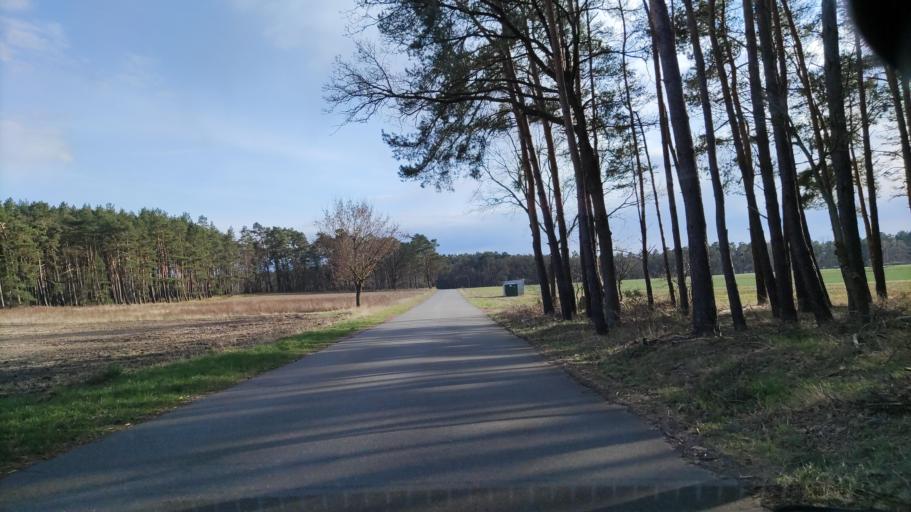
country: DE
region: Lower Saxony
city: Klein Gusborn
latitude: 53.0864
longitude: 11.2226
